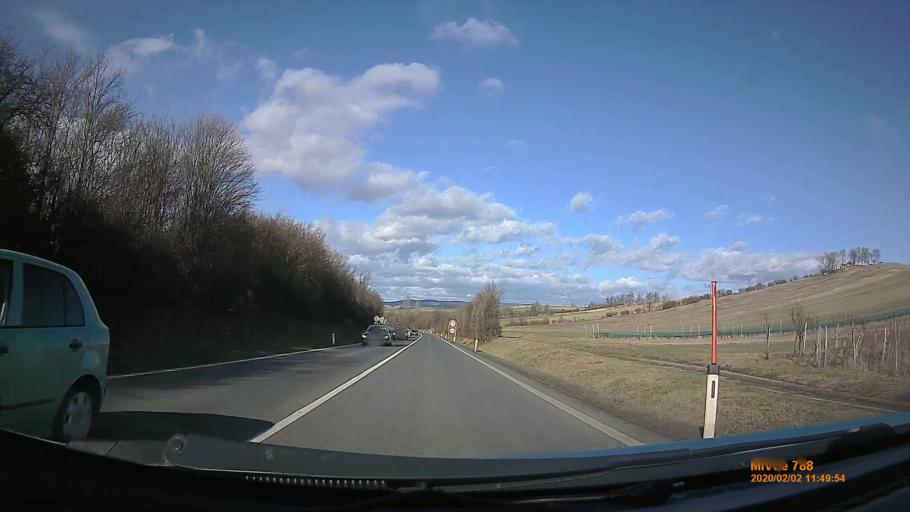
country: AT
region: Burgenland
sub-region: Eisenstadt-Umgebung
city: Klingenbach
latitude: 47.7572
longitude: 16.5455
